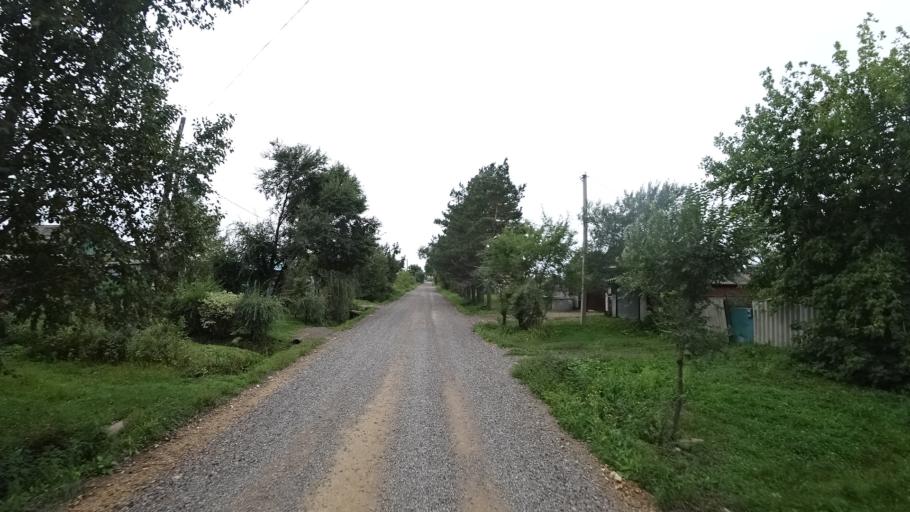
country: RU
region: Primorskiy
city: Chernigovka
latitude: 44.3411
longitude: 132.5640
